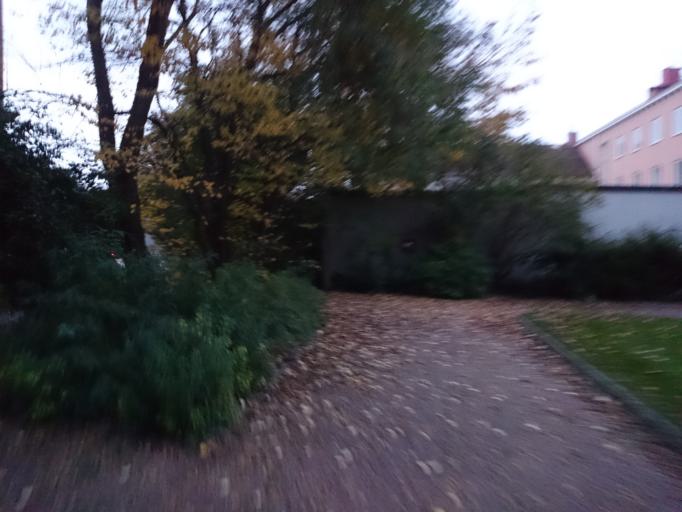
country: SE
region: Soedermanland
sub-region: Nykopings Kommun
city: Nykoping
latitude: 58.7529
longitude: 17.0102
